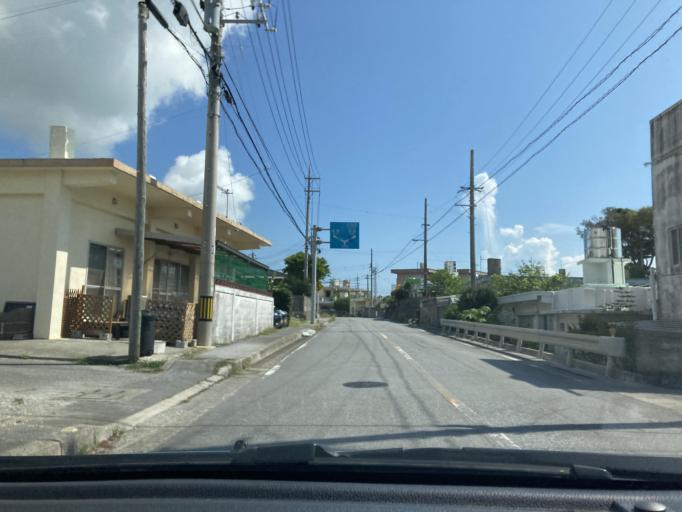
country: JP
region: Okinawa
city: Tomigusuku
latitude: 26.1404
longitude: 127.7907
